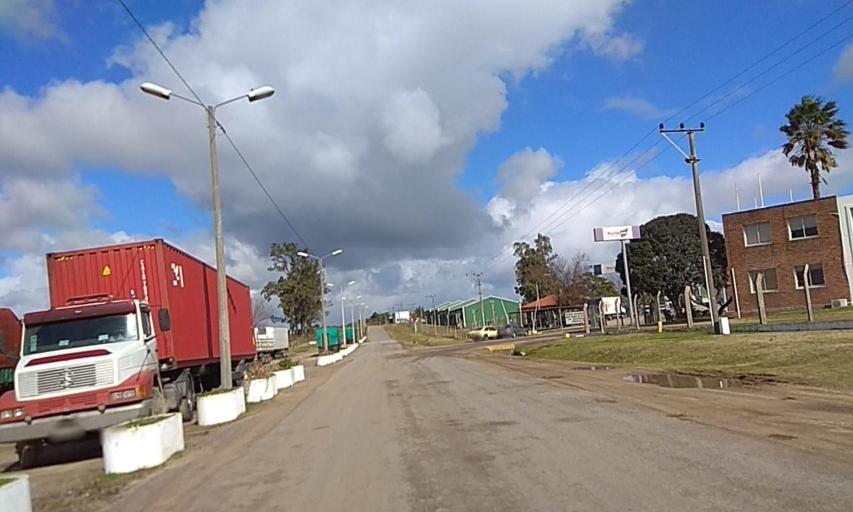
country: UY
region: Florida
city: Florida
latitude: -34.1118
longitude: -56.2266
